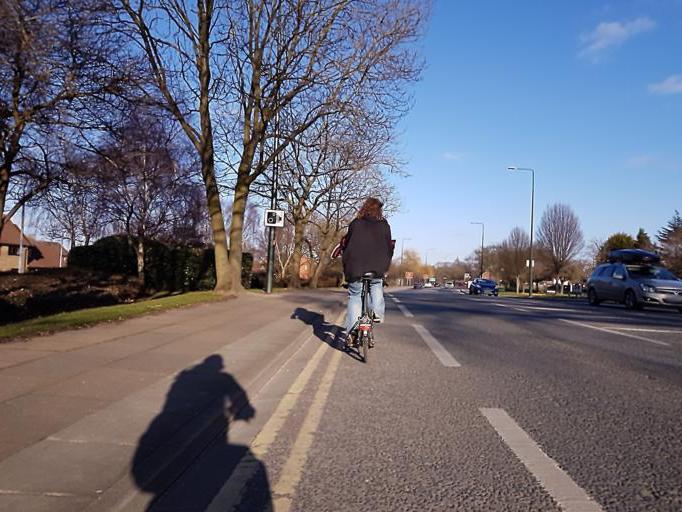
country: GB
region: England
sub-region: North East Lincolnshire
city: Grimsby
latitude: 53.5531
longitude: -0.0605
